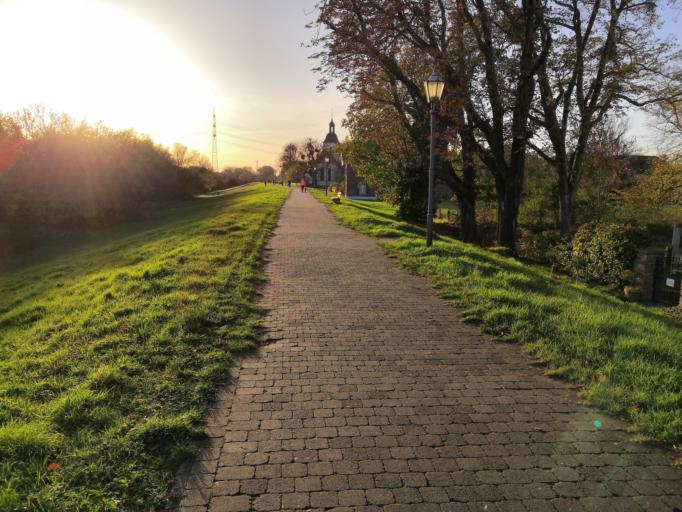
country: DE
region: North Rhine-Westphalia
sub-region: Regierungsbezirk Dusseldorf
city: Hochfeld
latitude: 51.3817
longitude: 6.7056
